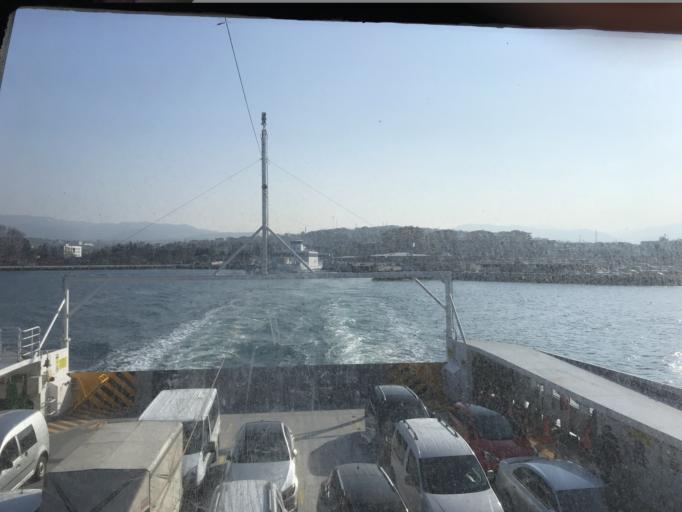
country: TR
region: Yalova
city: Yalova
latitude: 40.6635
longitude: 29.2790
